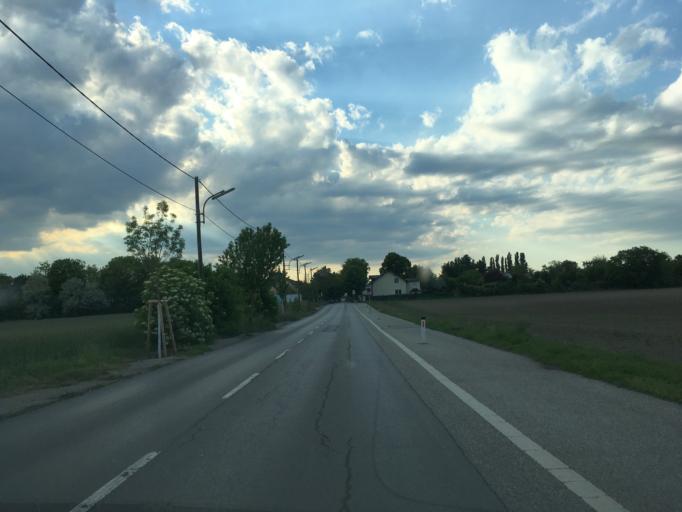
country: AT
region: Lower Austria
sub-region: Politischer Bezirk Wien-Umgebung
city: Gerasdorf bei Wien
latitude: 48.2817
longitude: 16.4891
